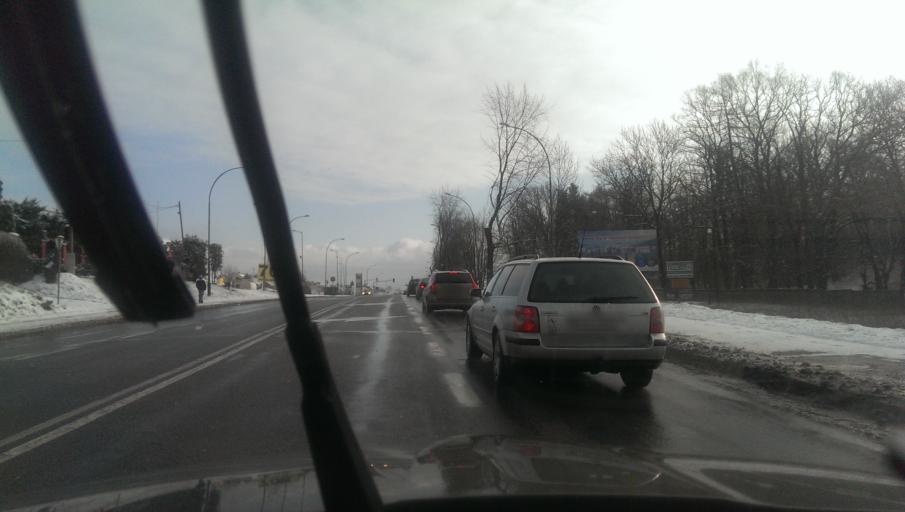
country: PL
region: Subcarpathian Voivodeship
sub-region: Powiat sanocki
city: Sanok
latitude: 49.5649
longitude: 22.1785
